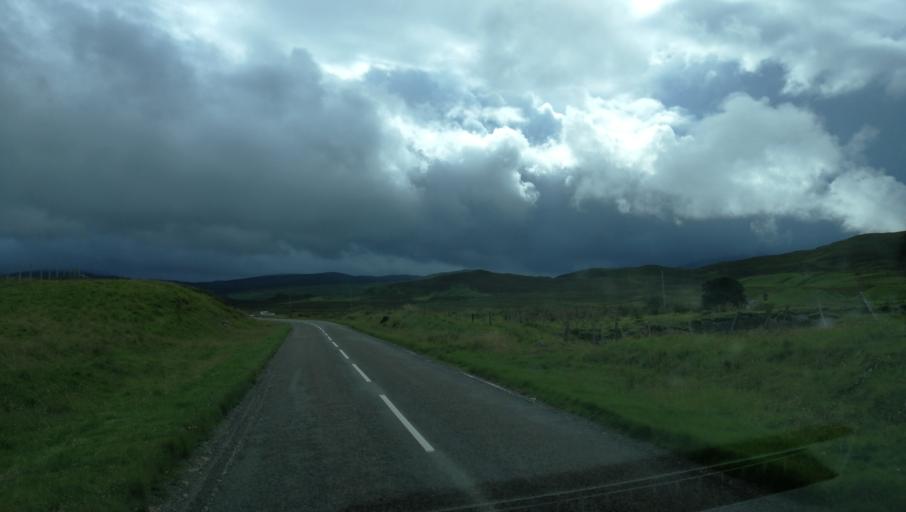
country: GB
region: Scotland
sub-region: Highland
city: Ullapool
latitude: 58.0754
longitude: -4.9765
